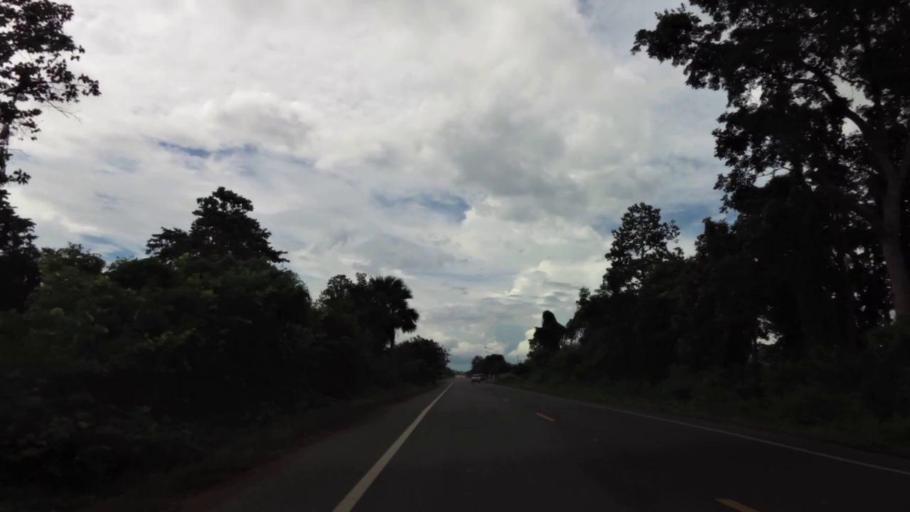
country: TH
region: Nakhon Sawan
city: Phai Sali
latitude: 15.5993
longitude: 100.6716
